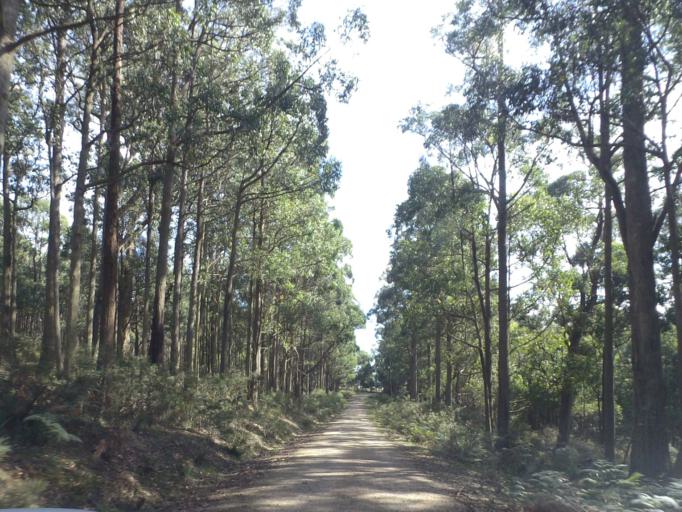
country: AU
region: Victoria
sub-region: Moorabool
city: Bacchus Marsh
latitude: -37.4244
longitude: 144.2488
